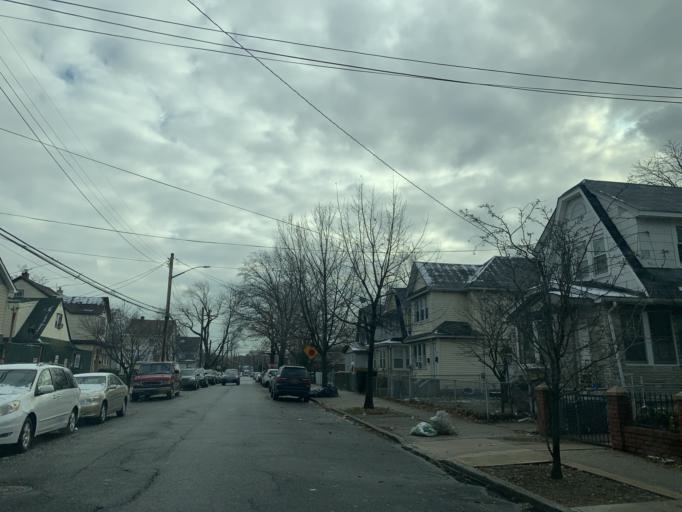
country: US
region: New York
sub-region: Queens County
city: Jamaica
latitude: 40.6883
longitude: -73.7802
